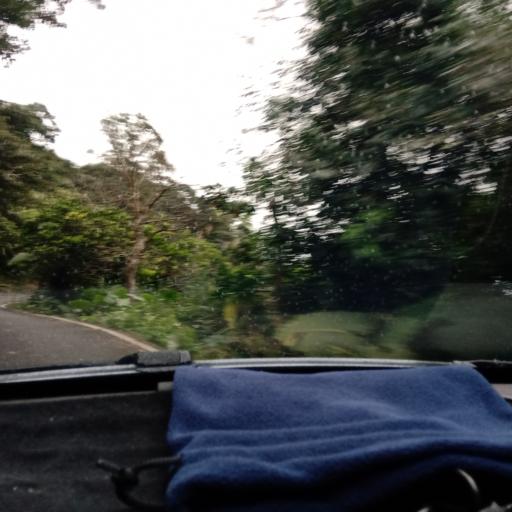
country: TW
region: Taiwan
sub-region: Yilan
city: Yilan
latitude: 24.8098
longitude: 121.7001
